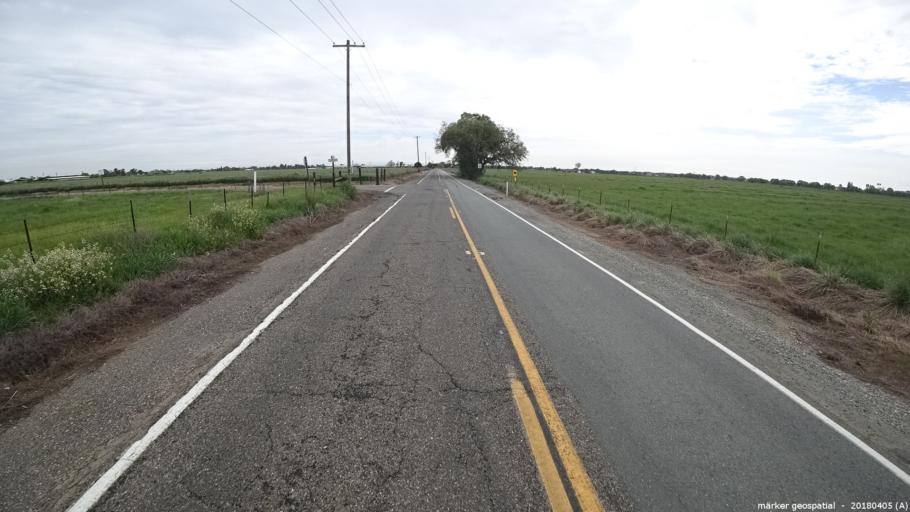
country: US
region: California
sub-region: Sacramento County
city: Galt
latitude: 38.2473
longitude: -121.3559
